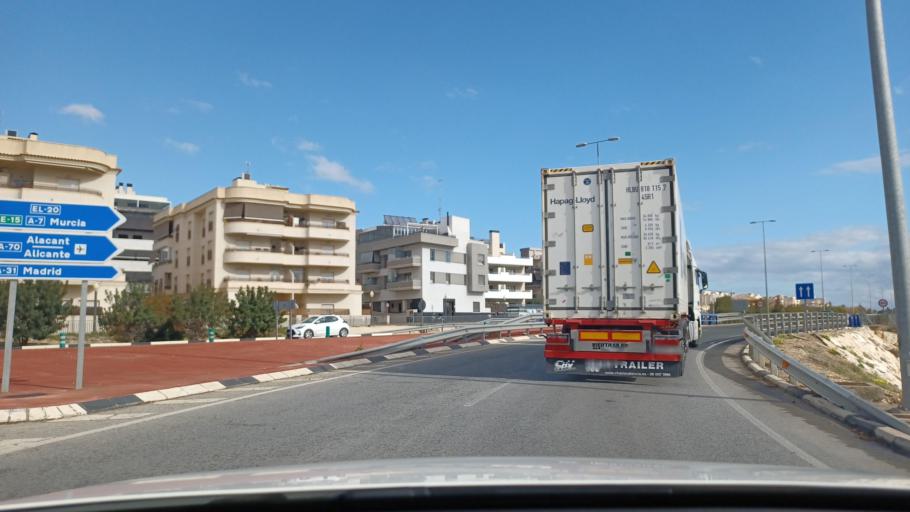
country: ES
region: Valencia
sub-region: Provincia de Alicante
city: Elche
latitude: 38.2598
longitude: -0.6719
